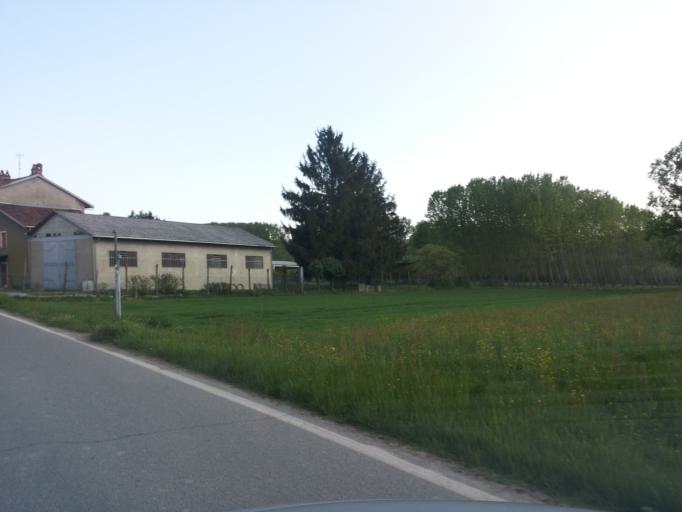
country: IT
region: Piedmont
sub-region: Provincia di Torino
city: Albiano d'Ivrea
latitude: 45.4406
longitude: 7.9673
